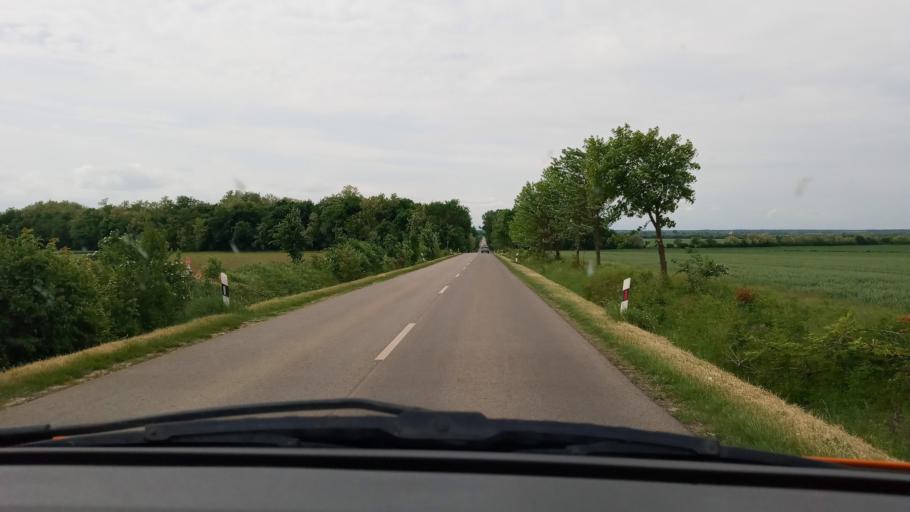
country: HU
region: Baranya
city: Vajszlo
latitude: 45.9295
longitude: 18.0653
